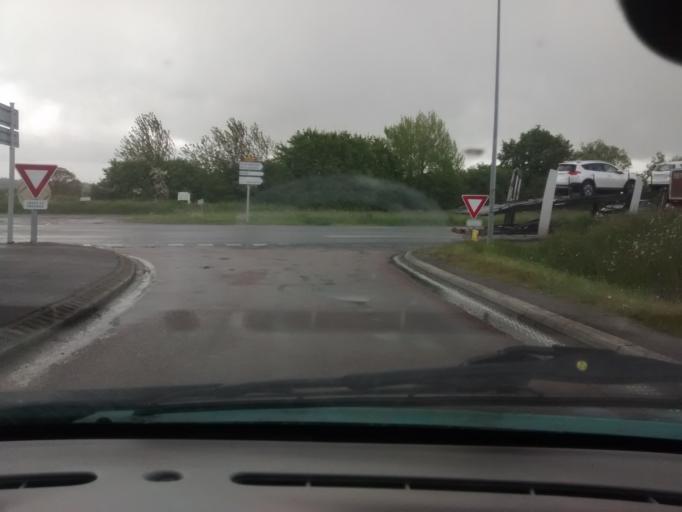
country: FR
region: Lower Normandy
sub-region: Departement de la Manche
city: Saint-Lo
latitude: 49.1103
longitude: -1.0554
